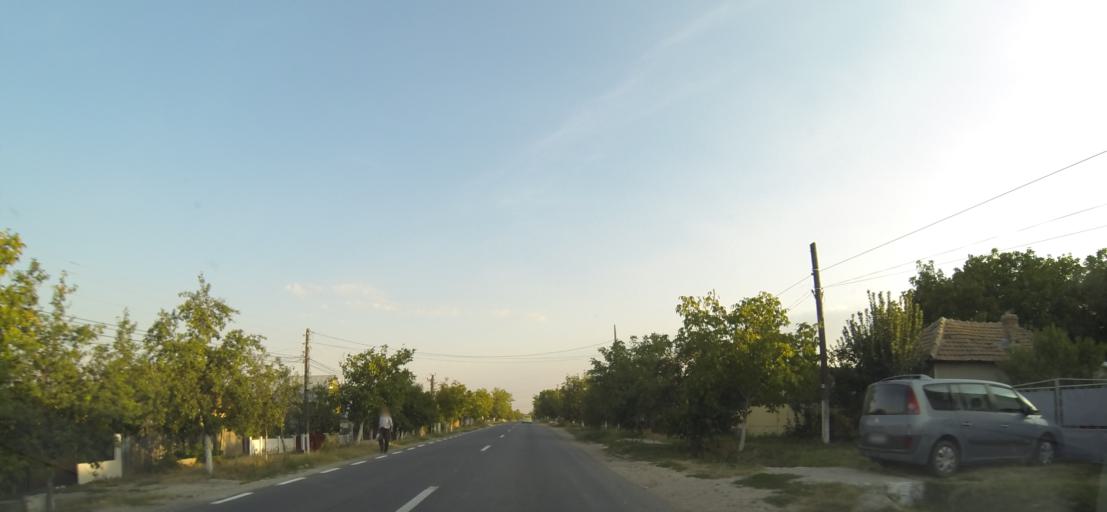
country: RO
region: Valcea
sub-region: Comuna Prundeni
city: Calina
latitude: 44.7183
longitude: 24.2519
